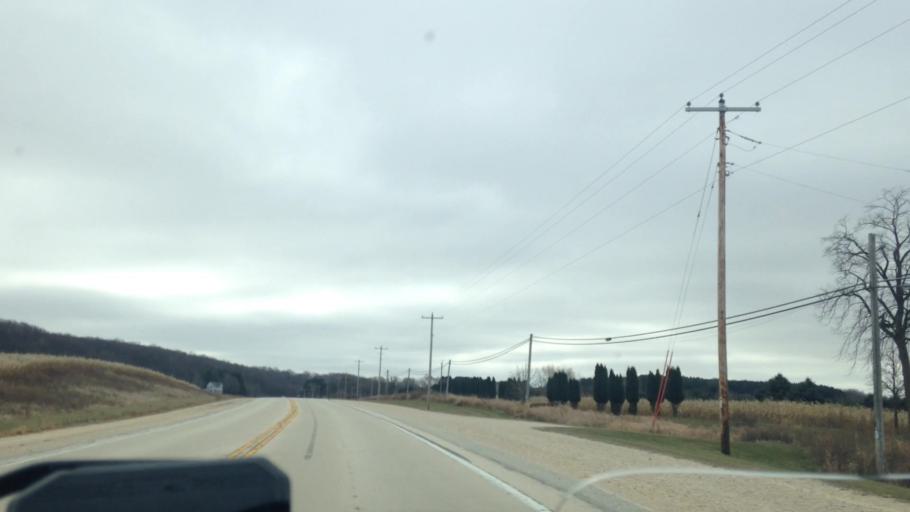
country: US
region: Wisconsin
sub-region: Dodge County
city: Mayville
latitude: 43.4643
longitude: -88.5460
